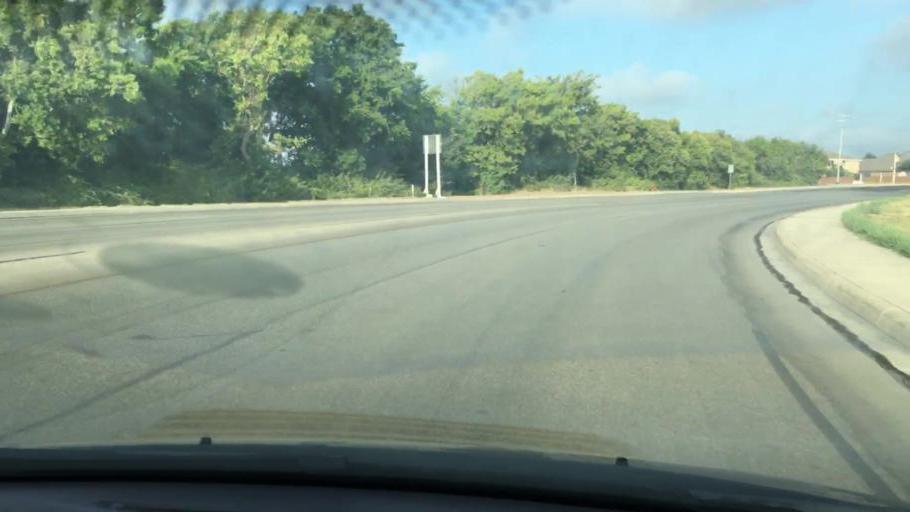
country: US
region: Texas
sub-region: Guadalupe County
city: Cibolo
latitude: 29.5721
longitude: -98.2366
